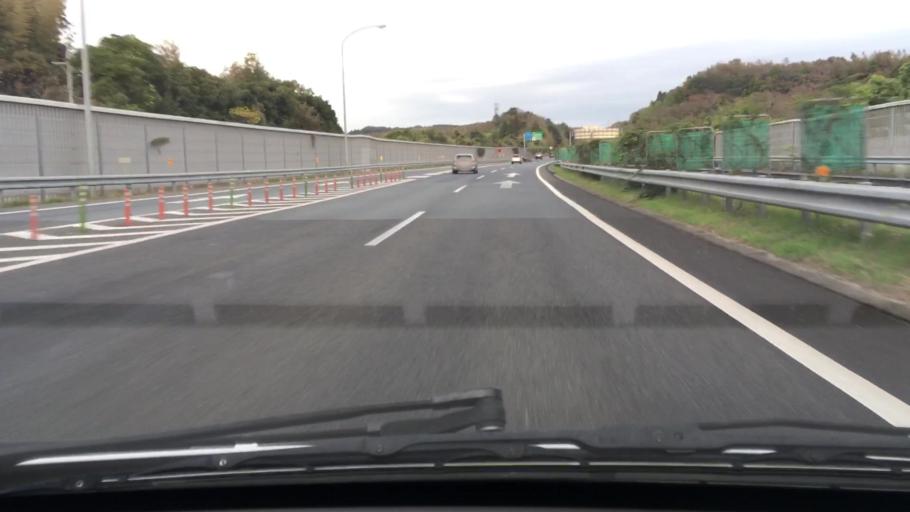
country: JP
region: Chiba
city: Kisarazu
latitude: 35.3809
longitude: 139.9861
